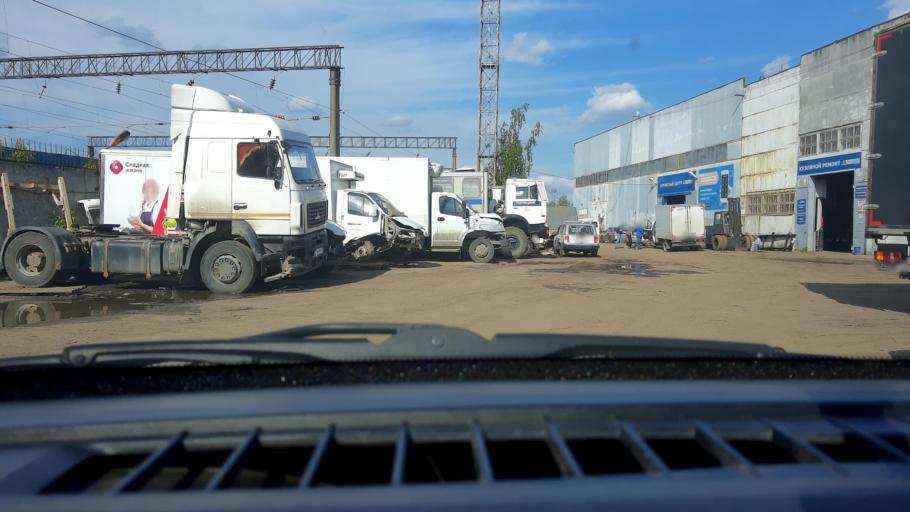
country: RU
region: Nizjnij Novgorod
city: Gorbatovka
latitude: 56.2523
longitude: 43.8769
